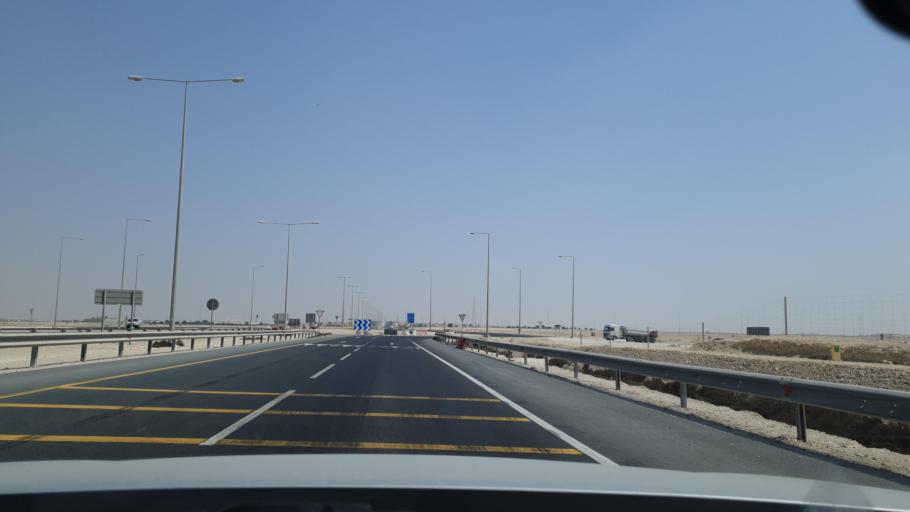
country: QA
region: Baladiyat az Za`ayin
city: Az Za`ayin
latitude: 25.6198
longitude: 51.3910
